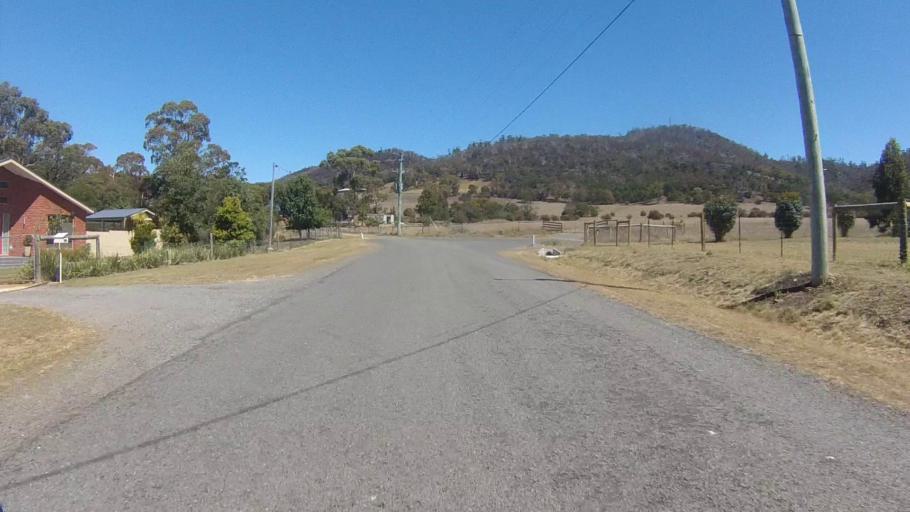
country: AU
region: Tasmania
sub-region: Clarence
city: Cambridge
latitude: -42.8493
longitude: 147.4632
